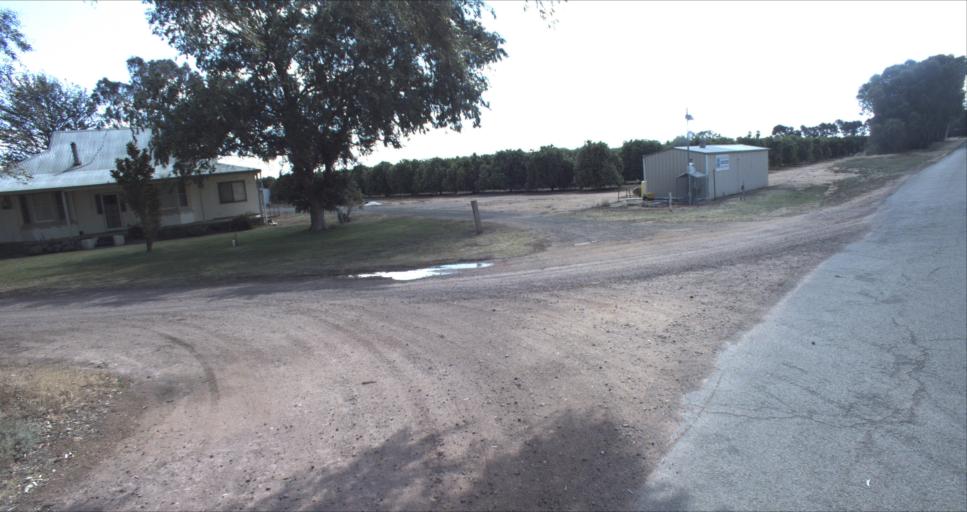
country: AU
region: New South Wales
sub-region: Leeton
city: Leeton
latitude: -34.5135
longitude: 146.2329
